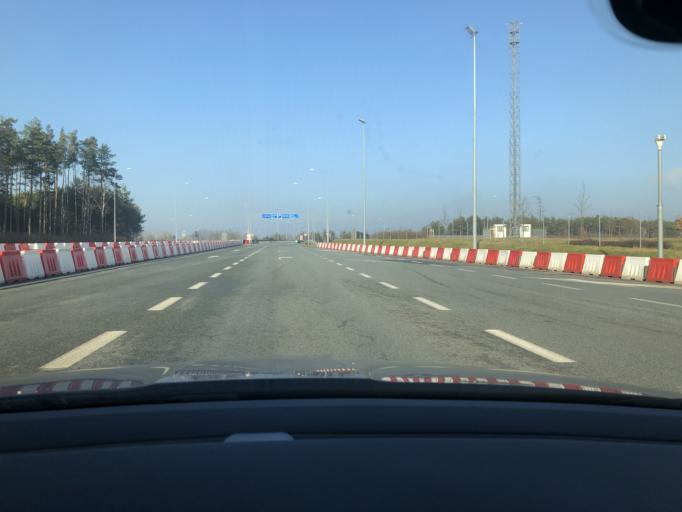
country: PL
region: Lubusz
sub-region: Powiat swiebodzinski
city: Swiebodzin
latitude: 52.3218
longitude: 15.5464
